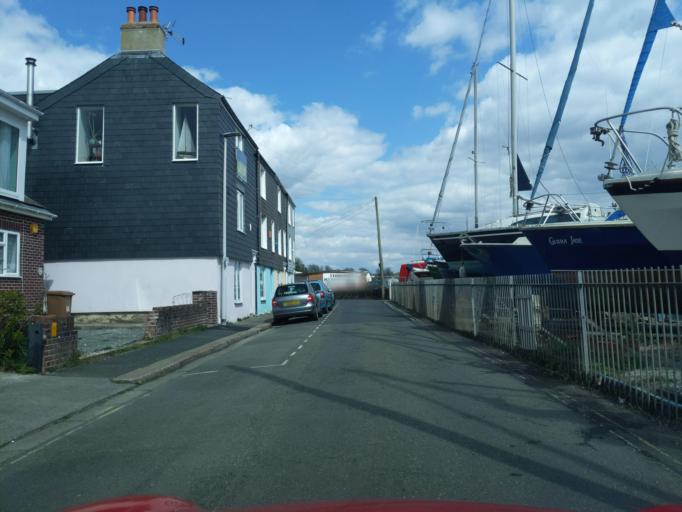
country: GB
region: England
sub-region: Cornwall
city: Millbrook
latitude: 50.3667
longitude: -4.1673
